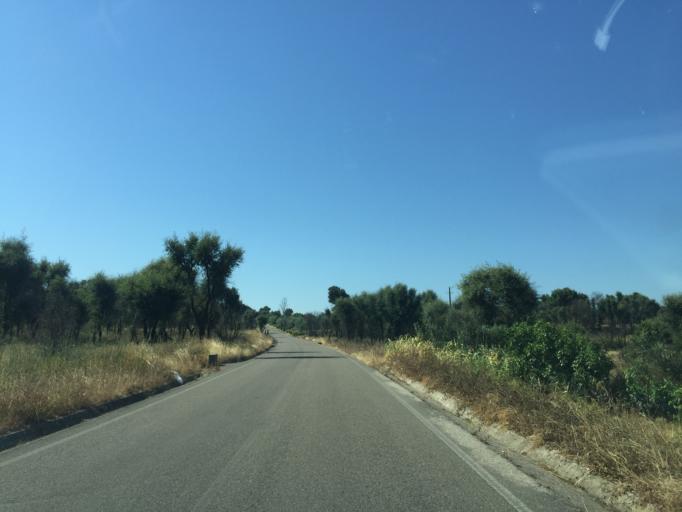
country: PT
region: Santarem
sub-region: Tomar
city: Tomar
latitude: 39.5929
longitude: -8.3284
